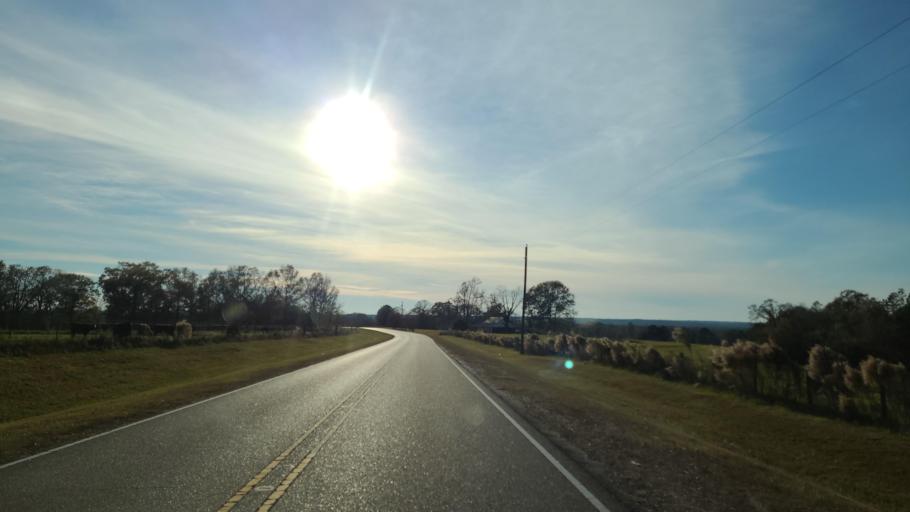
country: US
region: Mississippi
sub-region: Lamar County
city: Purvis
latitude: 31.1694
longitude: -89.3019
